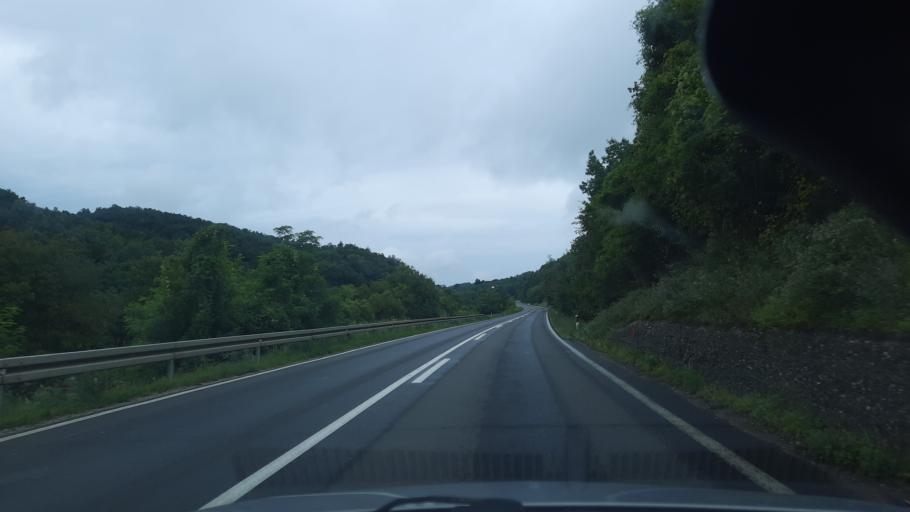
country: RS
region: Central Serbia
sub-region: Sumadijski Okrug
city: Knic
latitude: 43.9614
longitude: 20.8092
